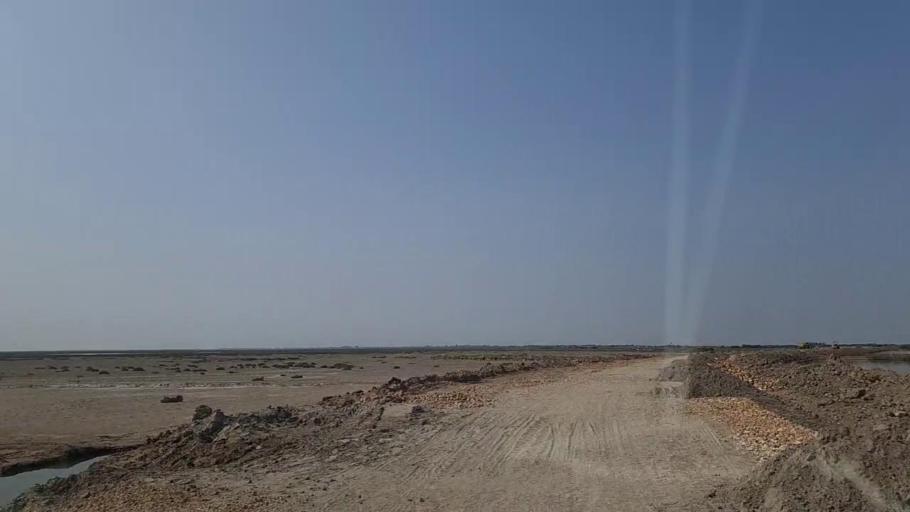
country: PK
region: Sindh
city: Chuhar Jamali
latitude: 24.1910
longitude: 67.8426
